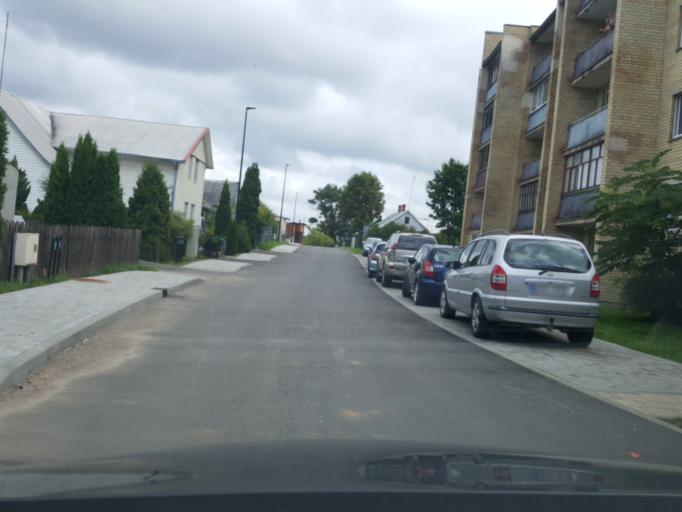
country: LT
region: Alytaus apskritis
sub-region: Alytus
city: Alytus
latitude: 54.3994
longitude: 24.0460
